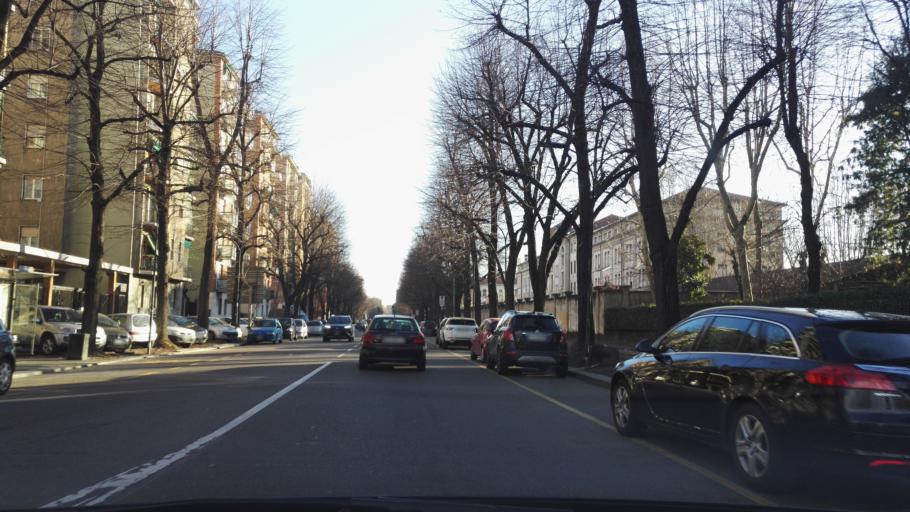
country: IT
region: Lombardy
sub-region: Citta metropolitana di Milano
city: Romano Banco
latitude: 45.4683
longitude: 9.1264
